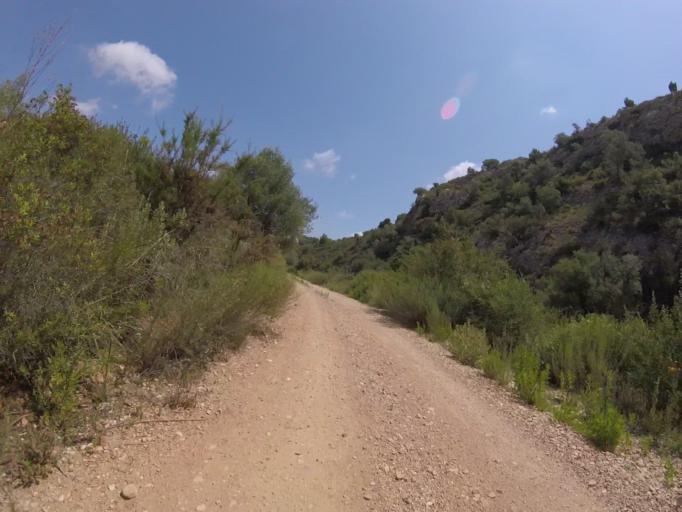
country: ES
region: Valencia
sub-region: Provincia de Castello
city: Torreblanca
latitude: 40.2067
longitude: 0.1383
